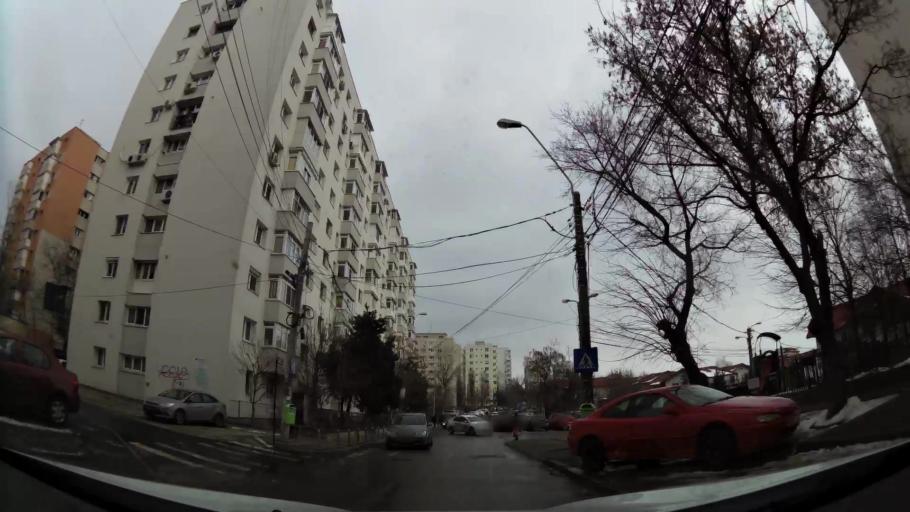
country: RO
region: Ilfov
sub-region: Comuna Popesti-Leordeni
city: Popesti-Leordeni
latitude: 44.4093
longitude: 26.1681
